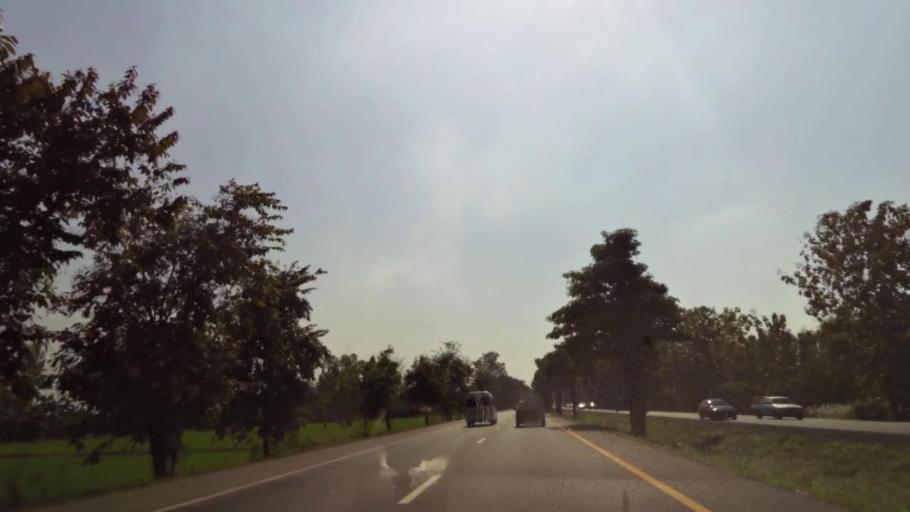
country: TH
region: Phichit
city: Bueng Na Rang
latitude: 16.0665
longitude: 100.1236
